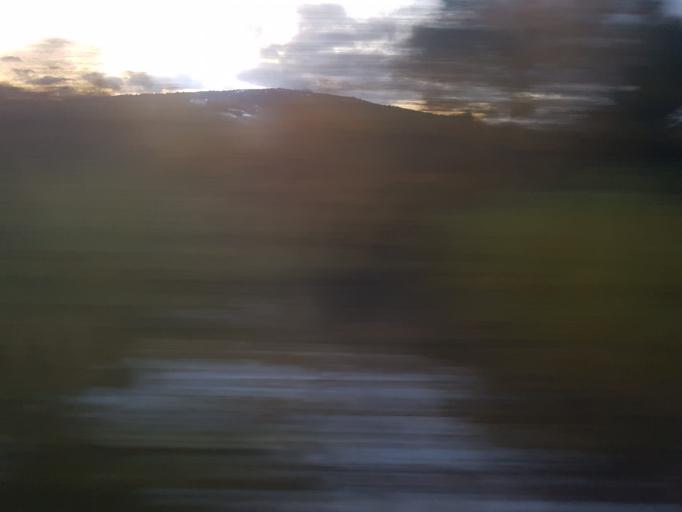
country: NO
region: Sor-Trondelag
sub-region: Oppdal
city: Oppdal
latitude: 62.5850
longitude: 9.6567
